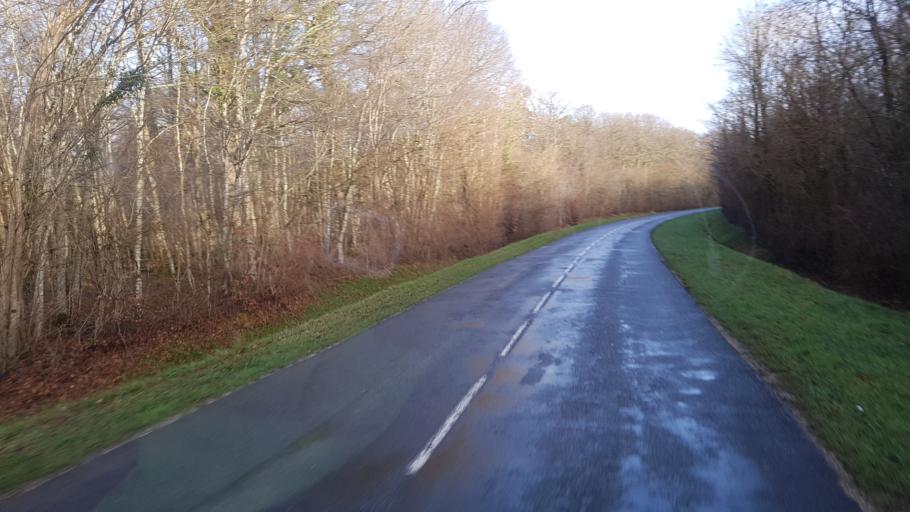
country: FR
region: Centre
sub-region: Departement du Loiret
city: Chilleurs-aux-Bois
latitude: 48.0148
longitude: 2.2025
